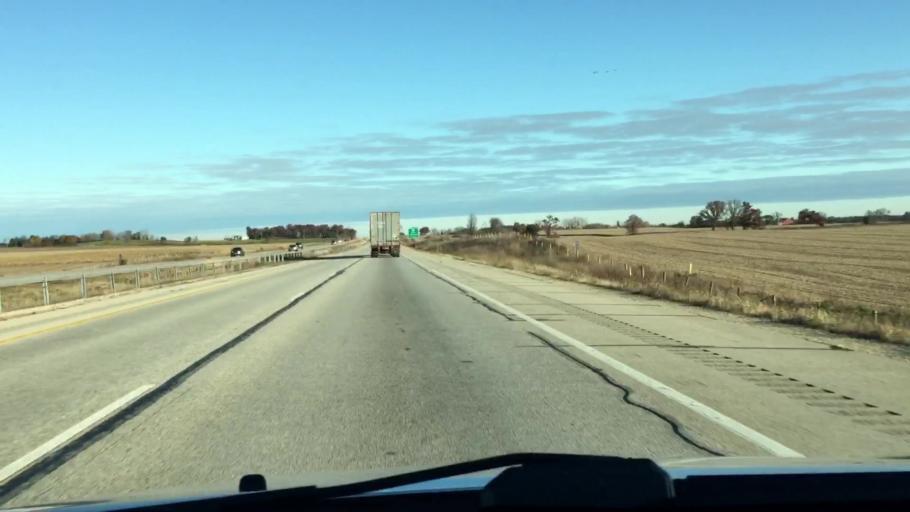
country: US
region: Wisconsin
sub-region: Dodge County
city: Lomira
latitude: 43.6636
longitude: -88.4415
